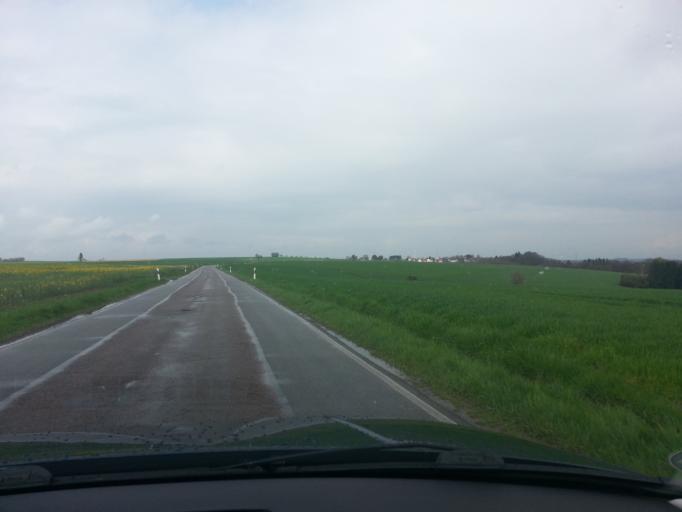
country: DE
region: Rheinland-Pfalz
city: Schmitshausen
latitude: 49.2934
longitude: 7.5191
